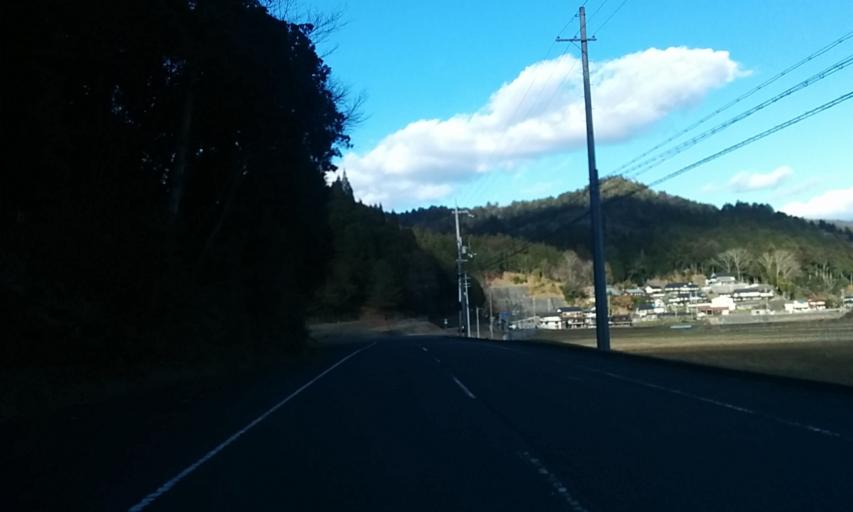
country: JP
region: Kyoto
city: Fukuchiyama
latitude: 35.2796
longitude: 135.0334
